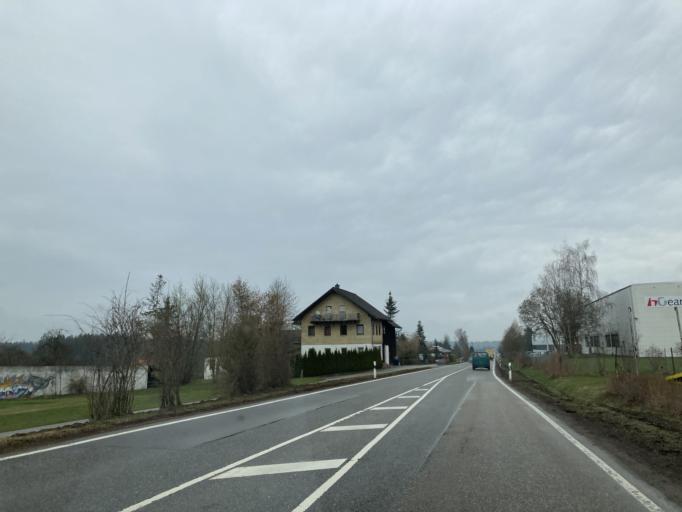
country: DE
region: Baden-Wuerttemberg
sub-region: Freiburg Region
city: Aichhalden
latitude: 48.2425
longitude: 8.4327
